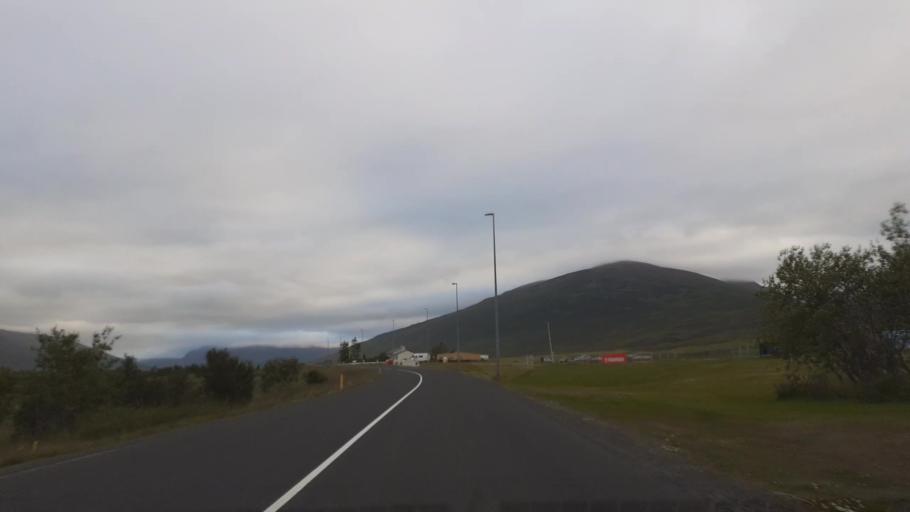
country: IS
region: Northeast
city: Dalvik
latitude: 65.9665
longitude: -18.5311
